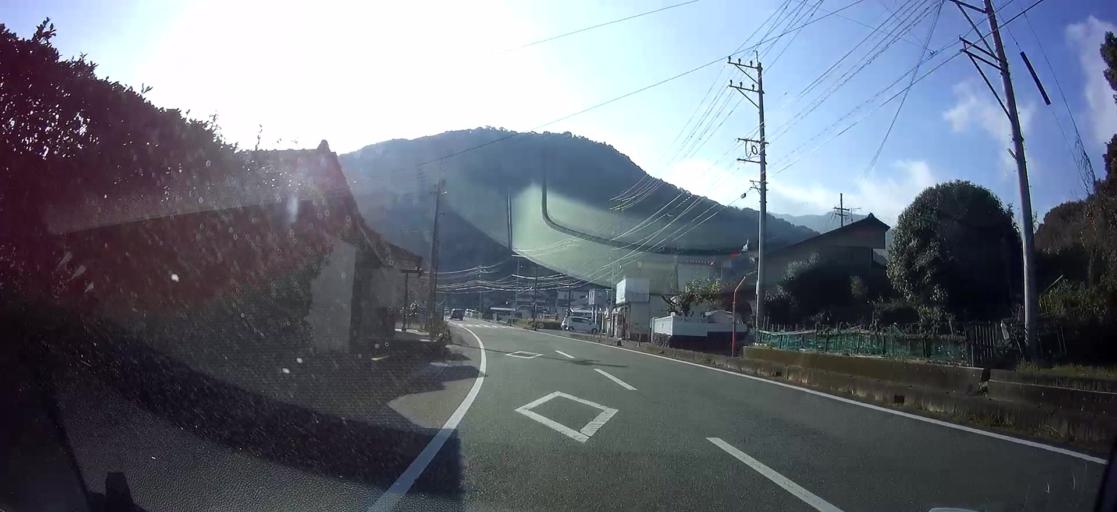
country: JP
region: Kumamoto
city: Minamata
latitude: 32.4096
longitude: 130.4053
